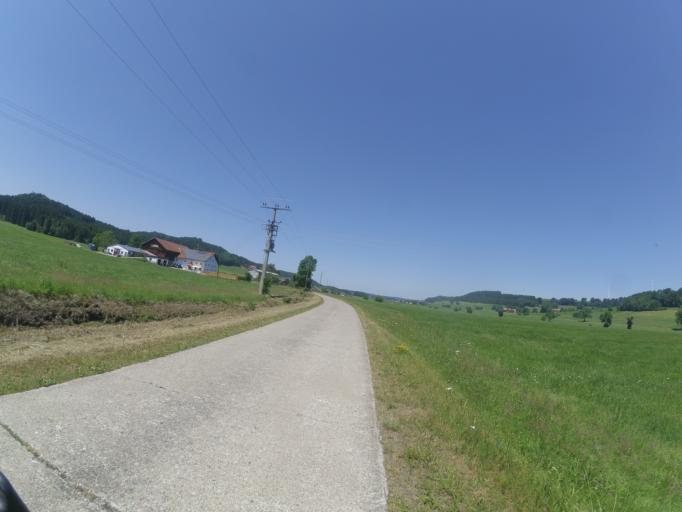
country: DE
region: Bavaria
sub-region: Swabia
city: Untrasried
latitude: 47.8624
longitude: 10.3495
